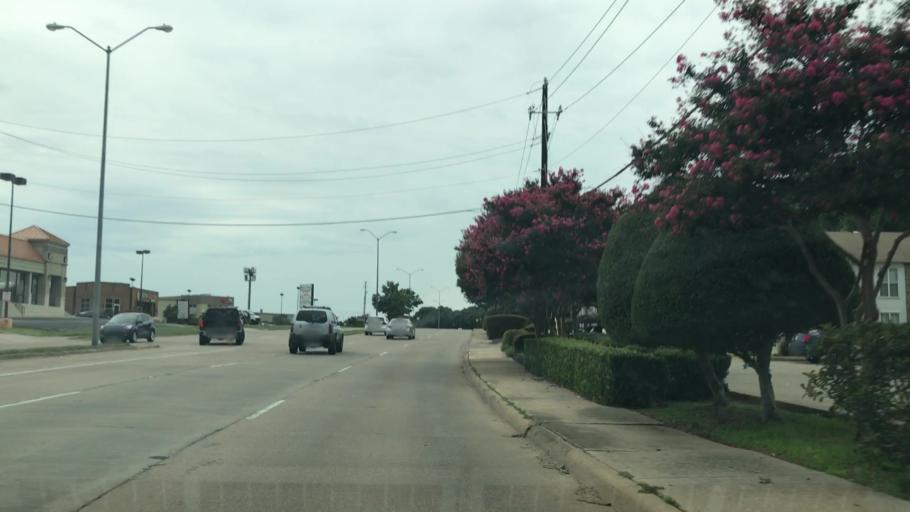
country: US
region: Texas
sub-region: Dallas County
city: Addison
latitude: 32.9508
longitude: -96.7996
